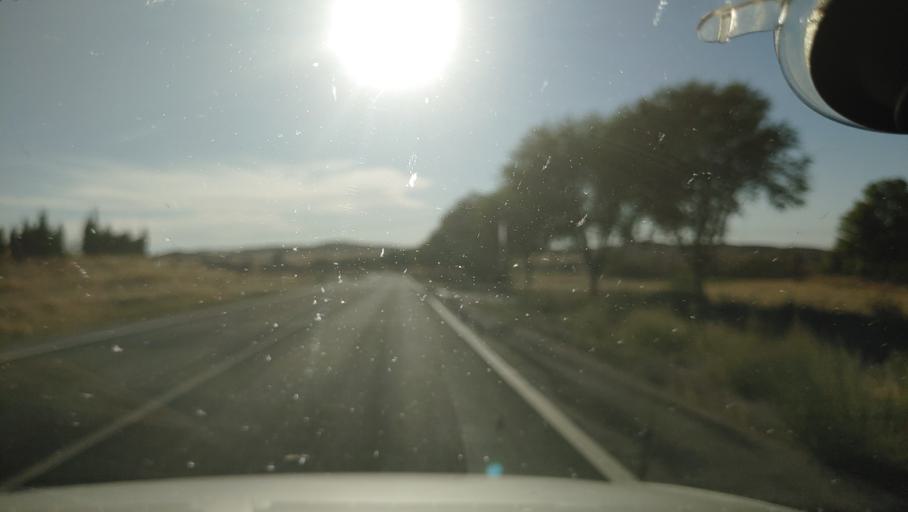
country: ES
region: Castille-La Mancha
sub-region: Provincia de Ciudad Real
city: Fuenllana
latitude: 38.7523
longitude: -2.9595
